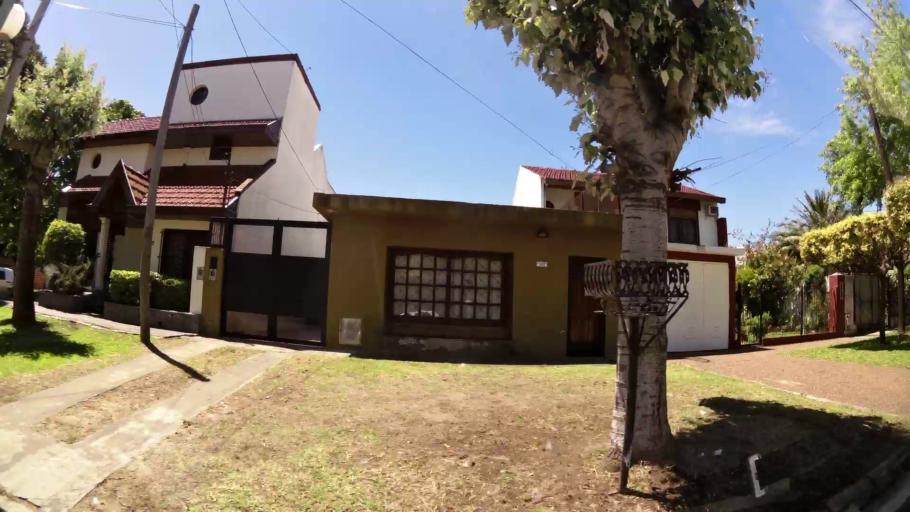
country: AR
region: Buenos Aires
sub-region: Partido de Quilmes
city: Quilmes
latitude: -34.7375
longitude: -58.2839
